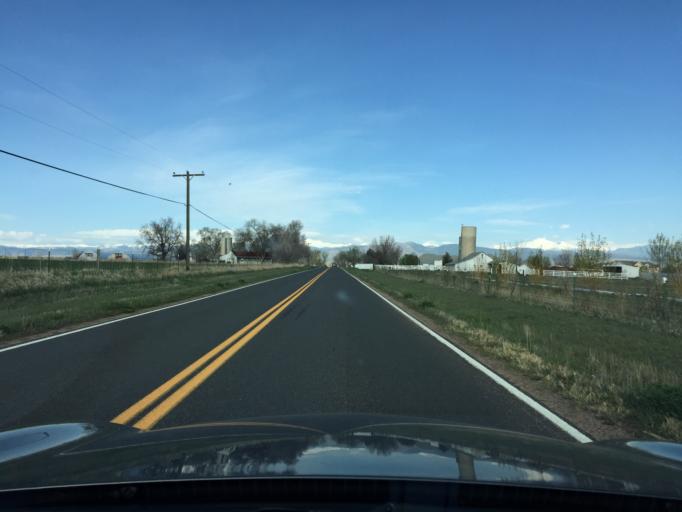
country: US
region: Colorado
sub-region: Boulder County
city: Longmont
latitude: 40.1162
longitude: -105.1129
